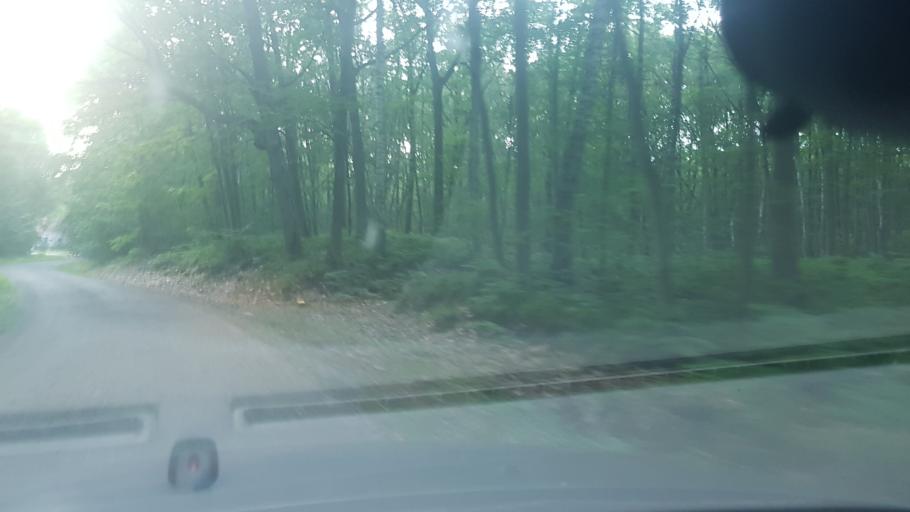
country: PL
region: Pomeranian Voivodeship
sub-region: Powiat nowodworski
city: Krynica Morska
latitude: 54.3573
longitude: 19.3425
